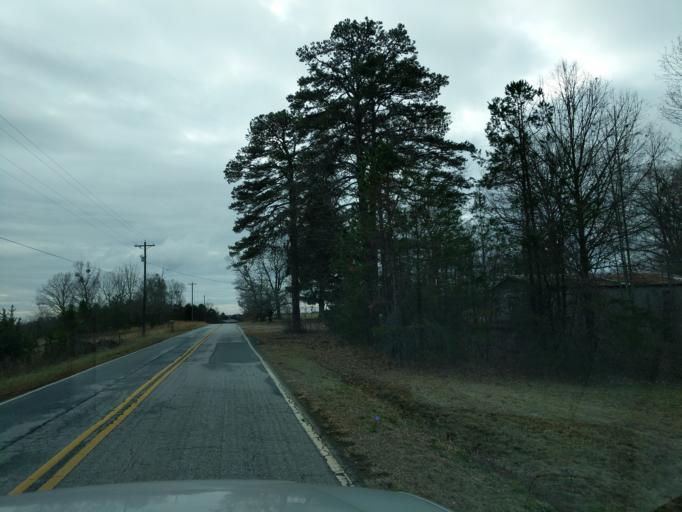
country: US
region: Georgia
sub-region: Rabun County
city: Clayton
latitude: 34.7839
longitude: -83.2519
